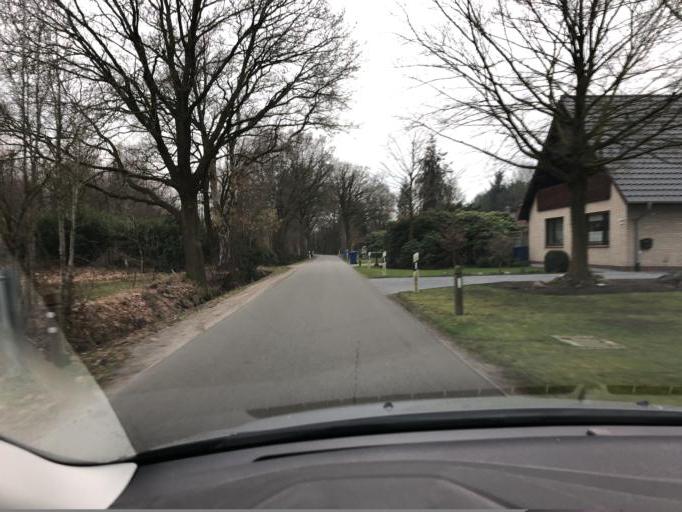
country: DE
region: Lower Saxony
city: Bad Zwischenahn
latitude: 53.1707
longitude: 8.0508
